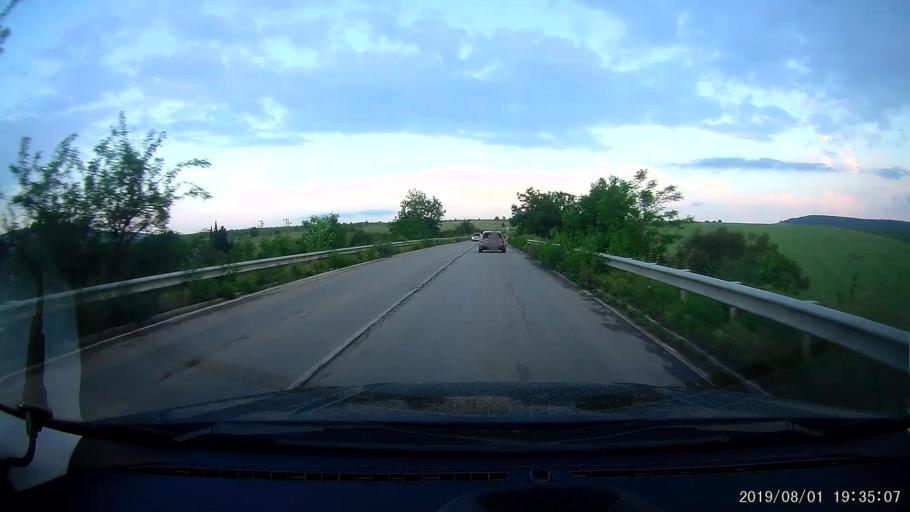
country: BG
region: Burgas
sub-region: Obshtina Sungurlare
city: Sungurlare
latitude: 42.7643
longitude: 26.8817
